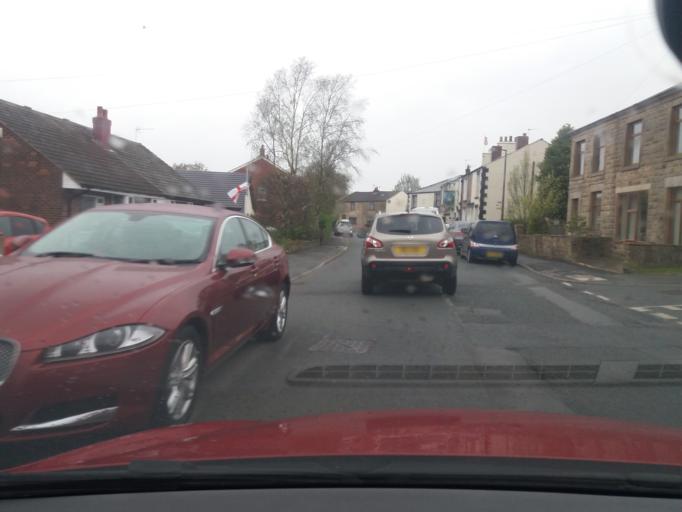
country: GB
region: England
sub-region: Lancashire
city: Clayton-le-Woods
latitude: 53.6943
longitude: -2.6339
